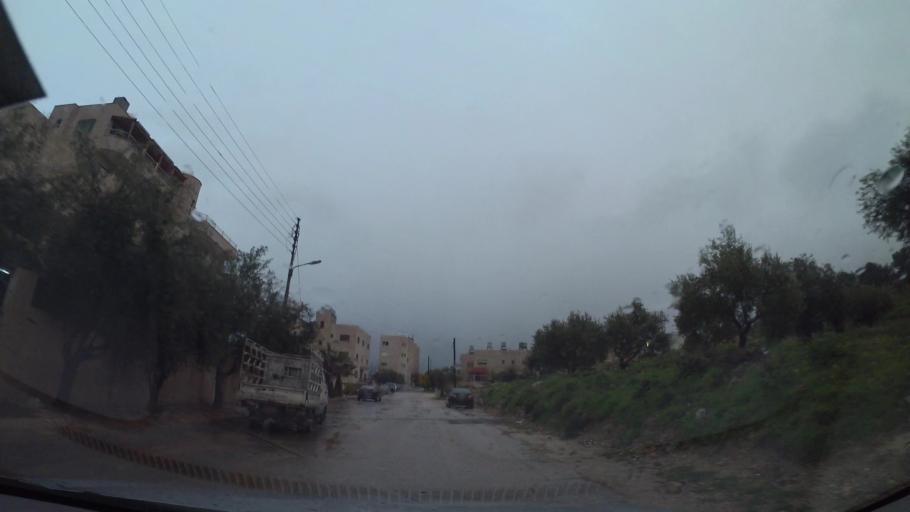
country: JO
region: Amman
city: Al Jubayhah
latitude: 32.0327
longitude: 35.8434
